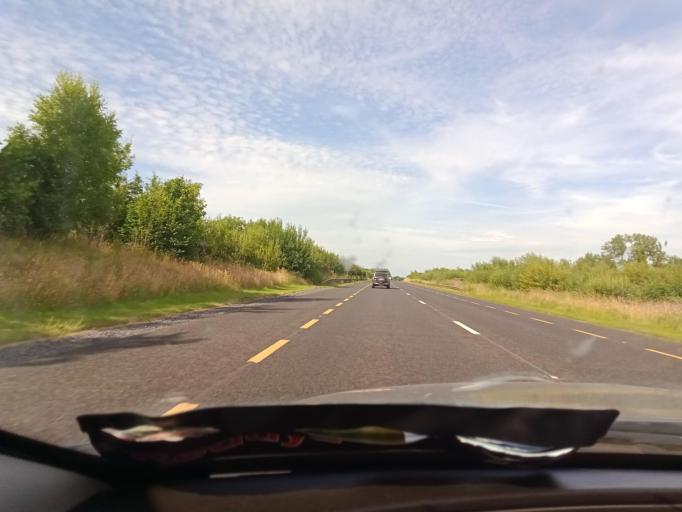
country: IE
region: Leinster
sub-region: An Iarmhi
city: An Muileann gCearr
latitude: 53.4818
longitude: -7.3484
